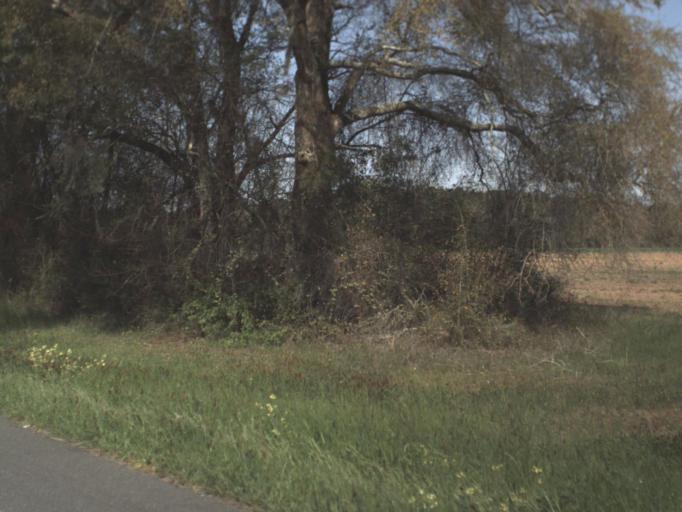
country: US
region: Florida
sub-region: Jackson County
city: Malone
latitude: 30.9455
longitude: -85.2692
